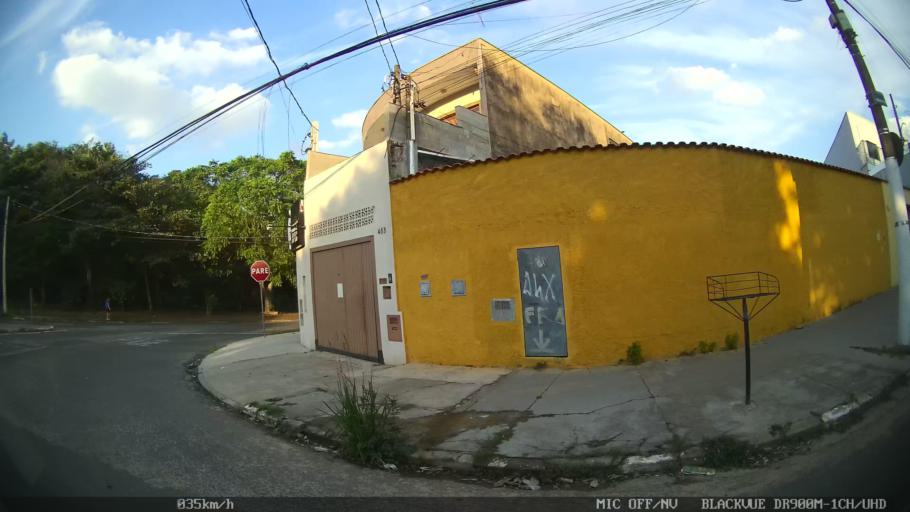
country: BR
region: Sao Paulo
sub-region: Hortolandia
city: Hortolandia
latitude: -22.8955
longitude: -47.1550
